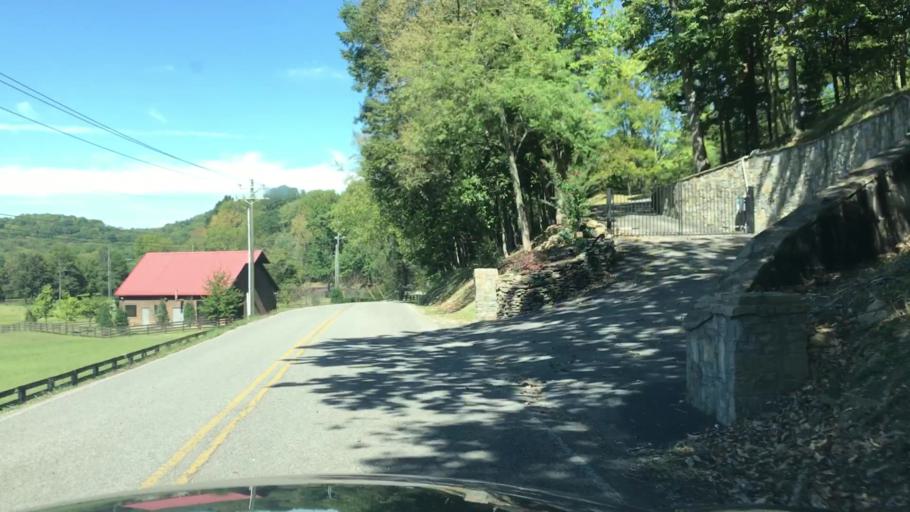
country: US
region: Tennessee
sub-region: Williamson County
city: Franklin
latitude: 35.9918
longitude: -86.8479
